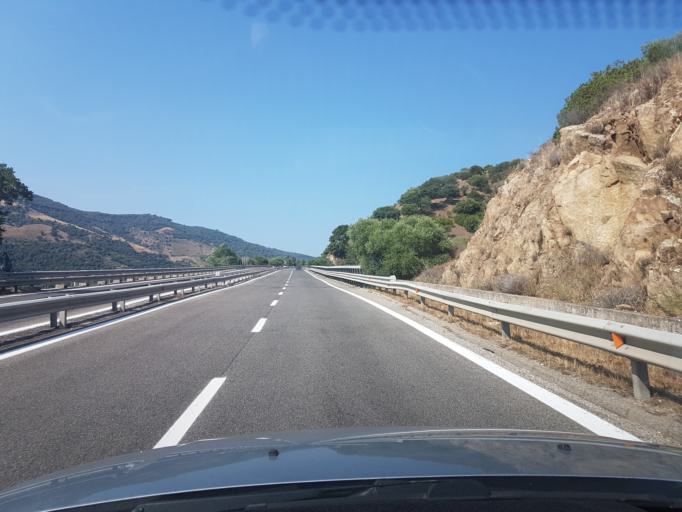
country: IT
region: Sardinia
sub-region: Provincia di Nuoro
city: Nuoro
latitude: 40.3473
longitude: 9.3280
